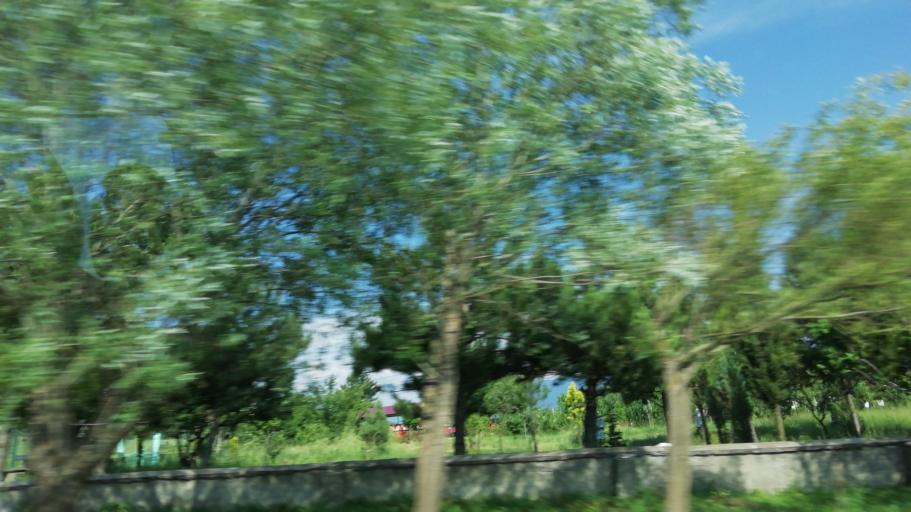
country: TR
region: Karabuk
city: Karabuk
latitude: 41.1015
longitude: 32.5950
